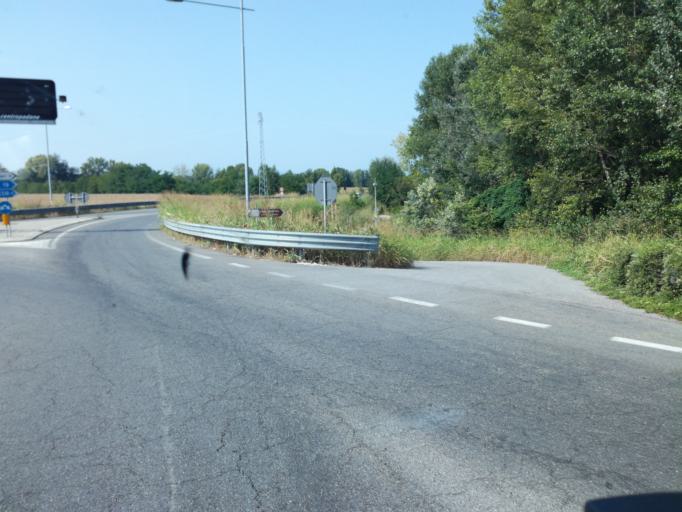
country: IT
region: Lombardy
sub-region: Provincia di Brescia
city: Capriano del Colle
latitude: 45.4707
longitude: 10.1189
